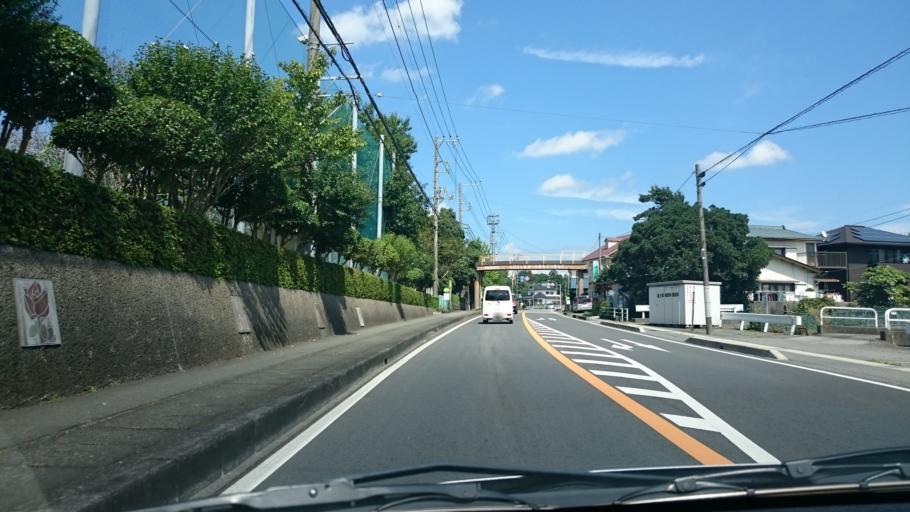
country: JP
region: Shizuoka
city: Gotemba
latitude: 35.2584
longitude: 138.9223
